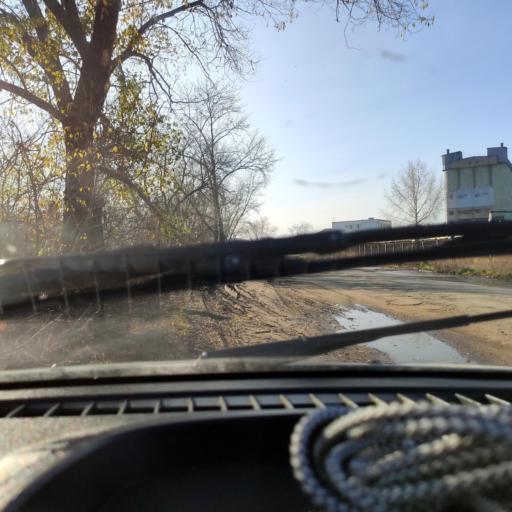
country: RU
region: Samara
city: Zhigulevsk
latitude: 53.4726
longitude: 49.5011
